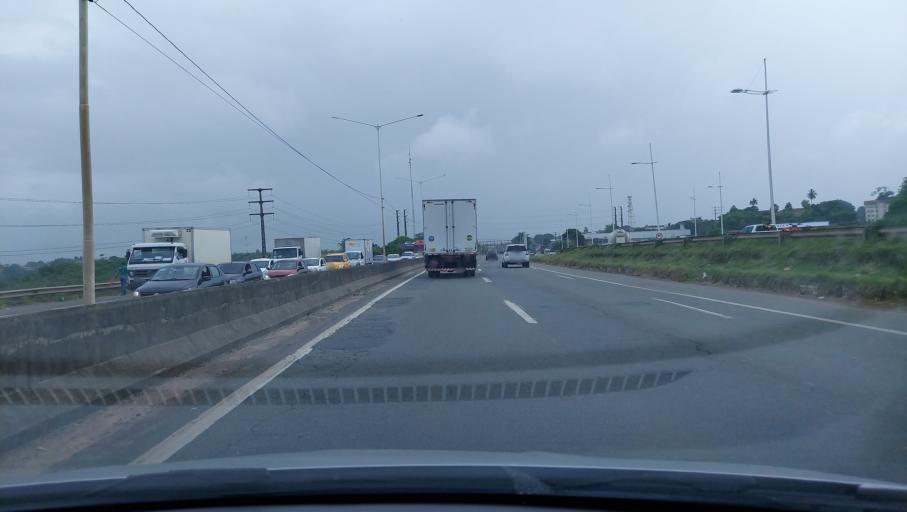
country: BR
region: Bahia
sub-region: Salvador
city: Salvador
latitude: -12.8898
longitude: -38.4438
